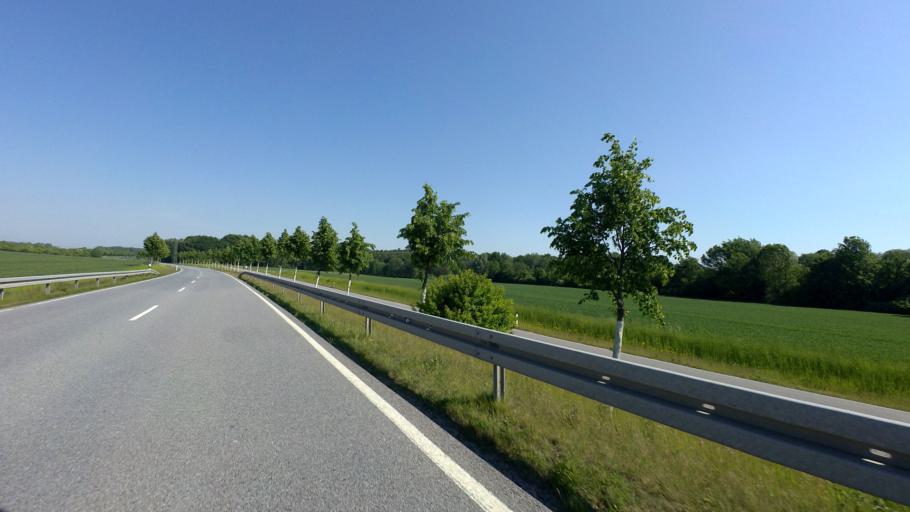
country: DE
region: Saxony
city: Nebelschutz
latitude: 51.2476
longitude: 14.1676
